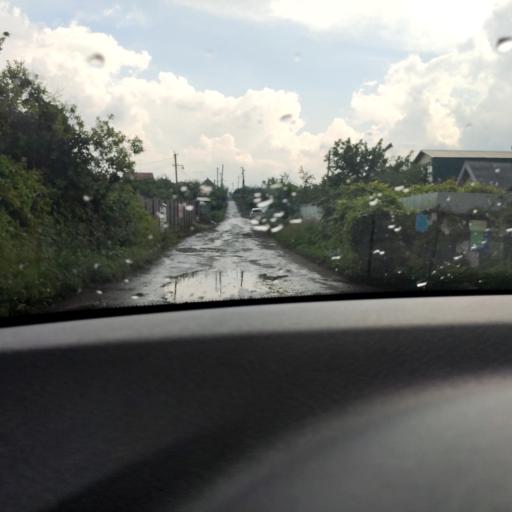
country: RU
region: Samara
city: Novosemeykino
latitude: 53.4039
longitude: 50.3160
